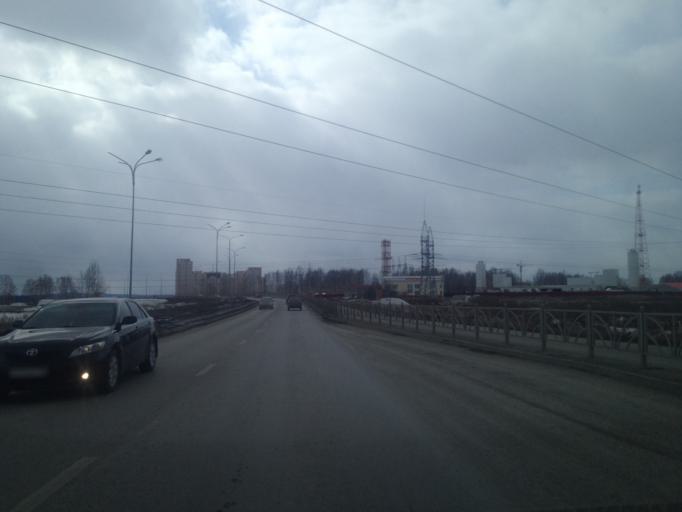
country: RU
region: Sverdlovsk
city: Sovkhoznyy
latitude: 56.7522
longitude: 60.5808
